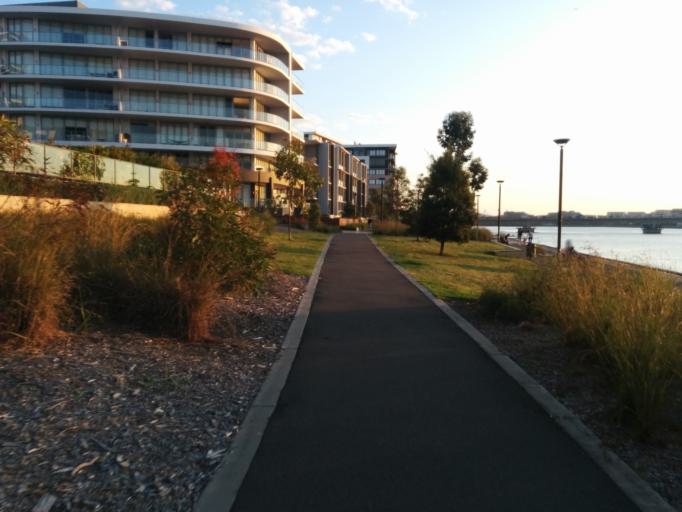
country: AU
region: New South Wales
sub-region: Canada Bay
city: Rhodes
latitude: -33.8255
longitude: 151.0853
